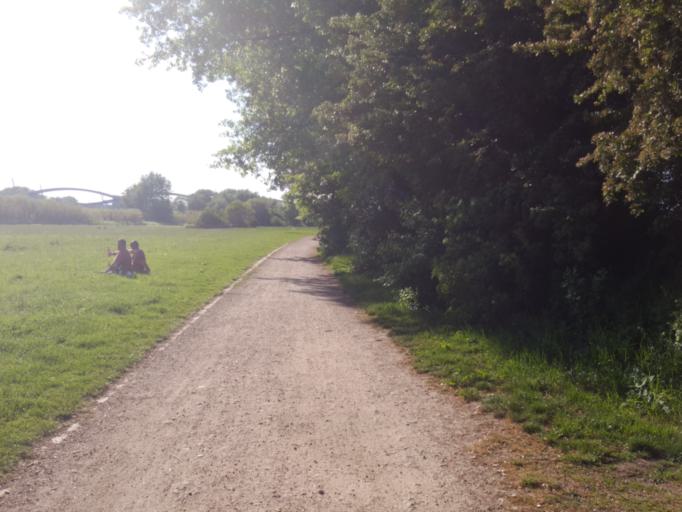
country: DE
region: Hamburg
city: Rothenburgsort
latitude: 53.5304
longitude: 10.0373
